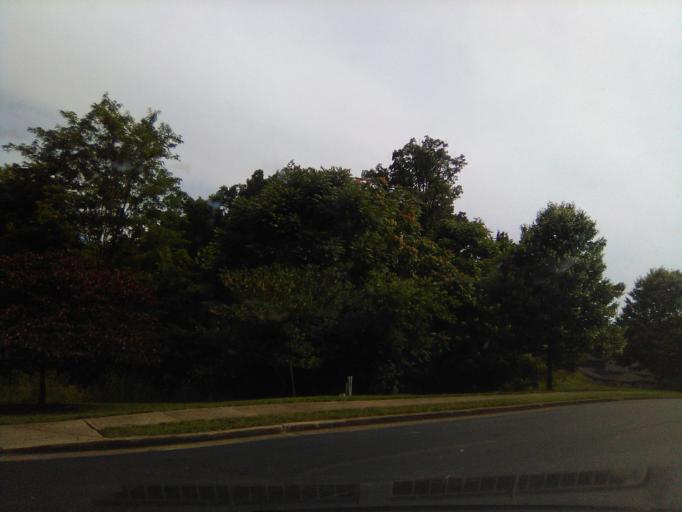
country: US
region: Tennessee
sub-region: Davidson County
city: Belle Meade
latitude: 36.0903
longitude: -86.9161
